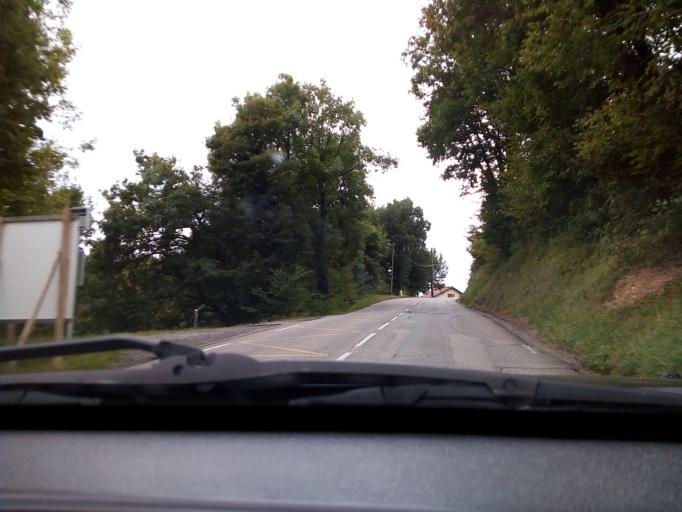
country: FR
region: Rhone-Alpes
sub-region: Departement de l'Isere
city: Corenc
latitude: 45.2266
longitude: 5.7654
